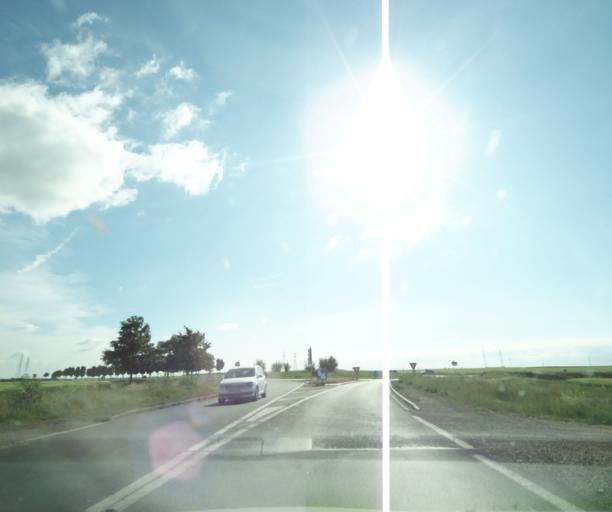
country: FR
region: Centre
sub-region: Departement d'Eure-et-Loir
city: Janville
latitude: 48.2076
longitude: 1.8222
